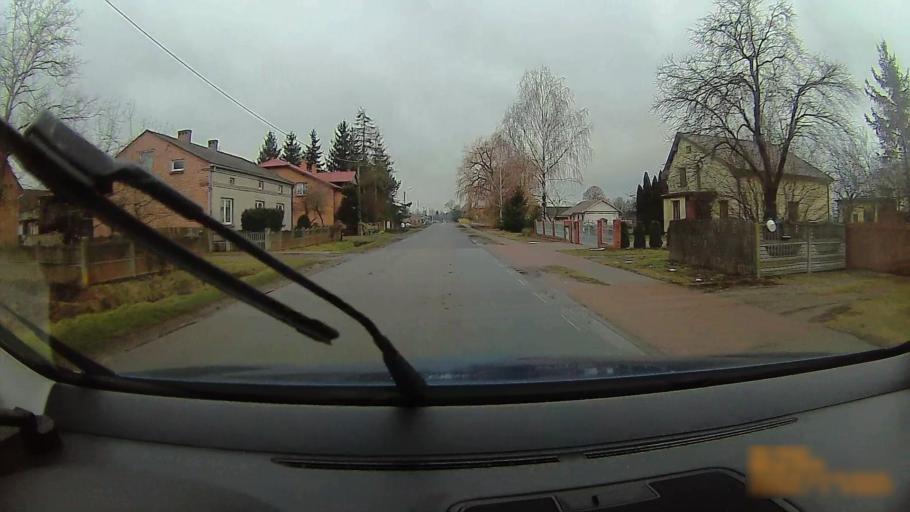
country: PL
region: Greater Poland Voivodeship
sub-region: Powiat koninski
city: Rychwal
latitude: 52.0956
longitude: 18.1622
